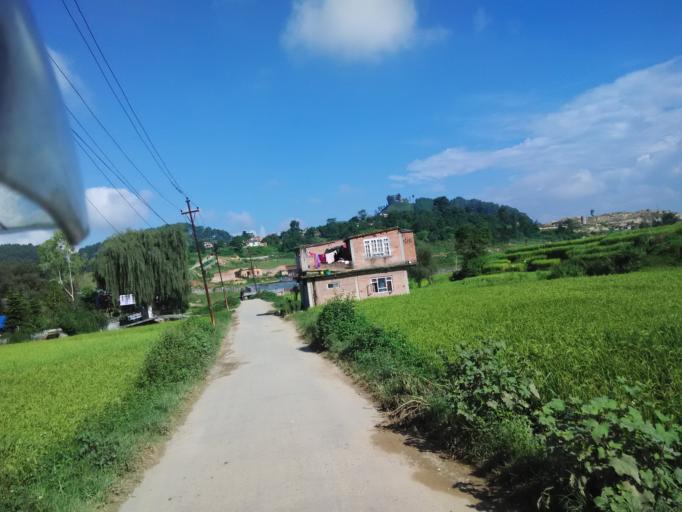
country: NP
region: Central Region
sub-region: Bagmati Zone
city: Patan
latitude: 27.6062
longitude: 85.3501
